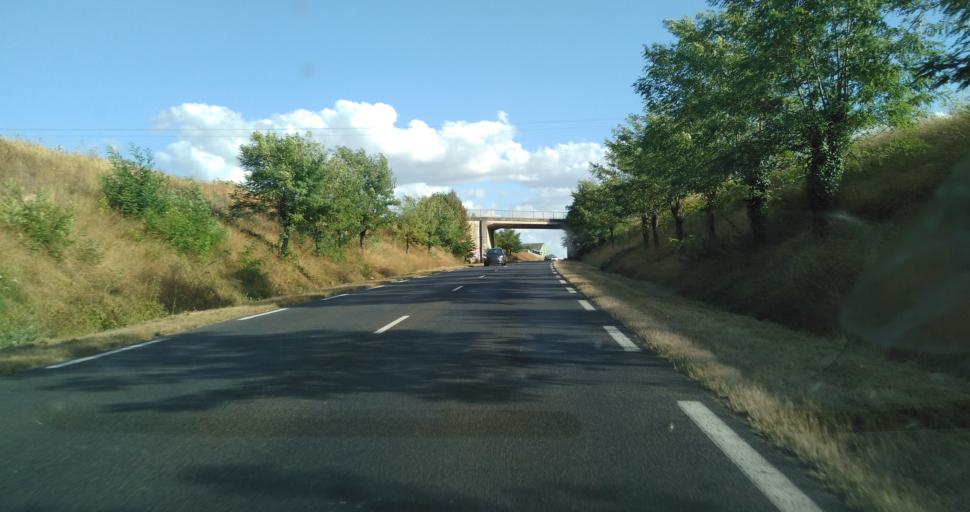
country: FR
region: Centre
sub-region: Departement d'Indre-et-Loire
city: Charge
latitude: 47.4205
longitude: 1.0147
